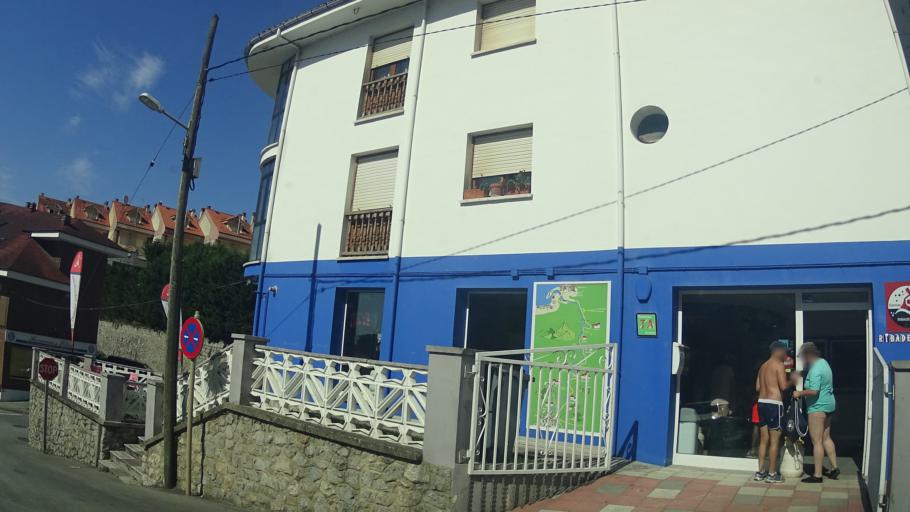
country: ES
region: Asturias
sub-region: Province of Asturias
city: Ribadesella
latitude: 43.4595
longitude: -5.0589
